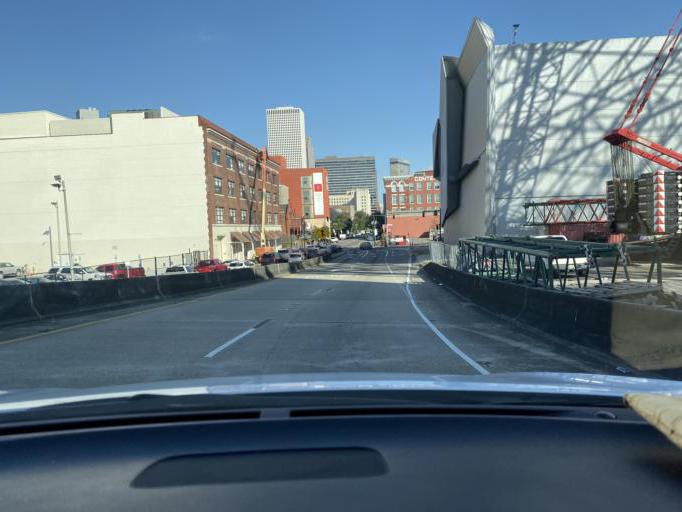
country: US
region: Louisiana
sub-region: Orleans Parish
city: New Orleans
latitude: 29.9421
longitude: -90.0713
